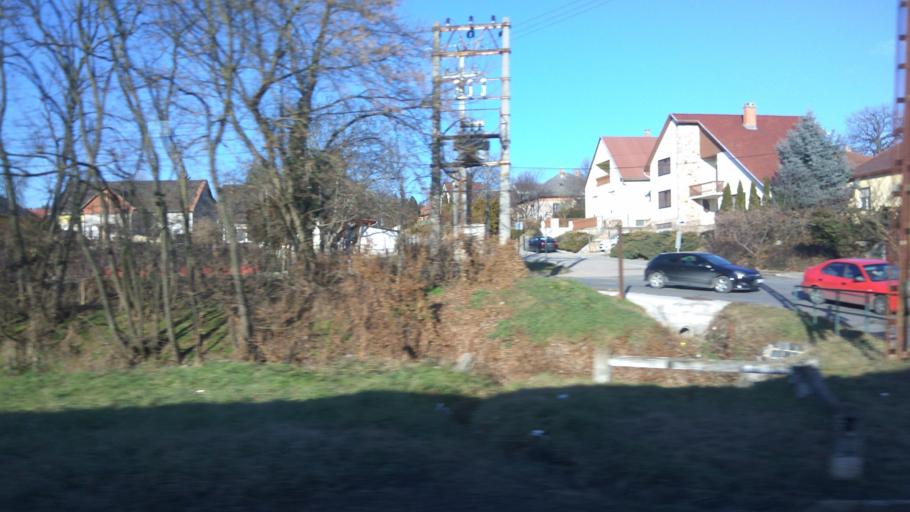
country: HU
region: Pest
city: Pecel
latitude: 47.4937
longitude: 19.3443
